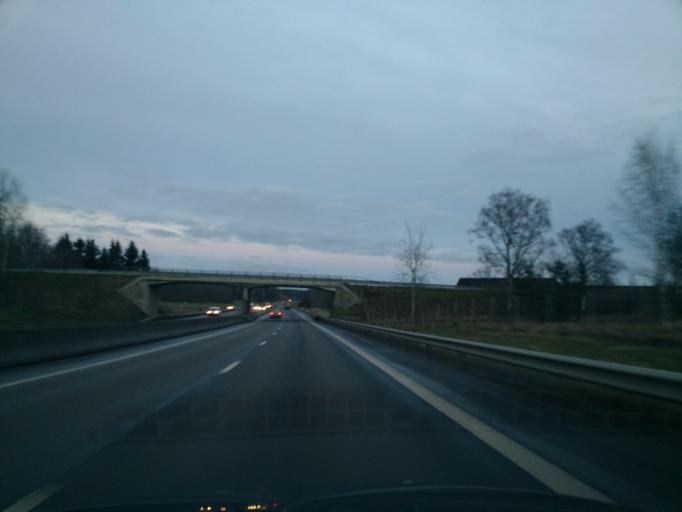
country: SE
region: OEstergoetland
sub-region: Norrkopings Kommun
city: Kimstad
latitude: 58.5243
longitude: 16.0097
